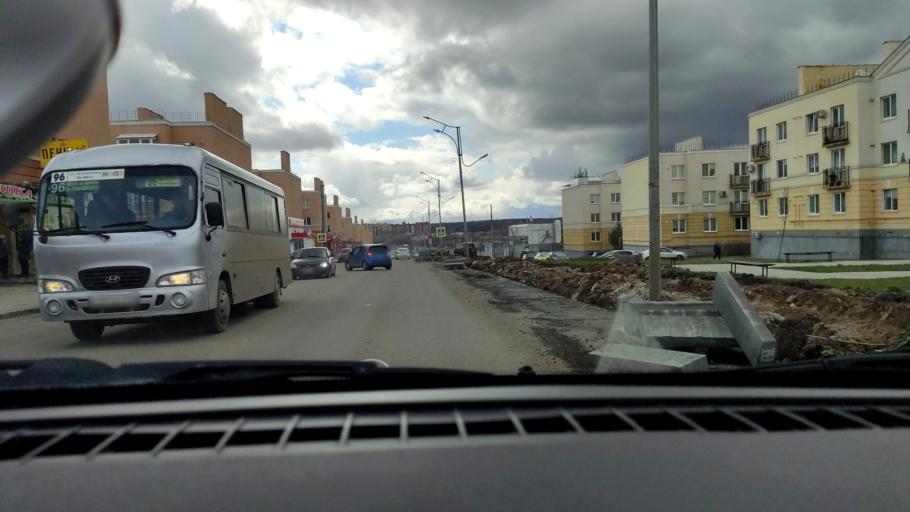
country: RU
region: Samara
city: Petra-Dubrava
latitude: 53.3132
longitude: 50.3139
